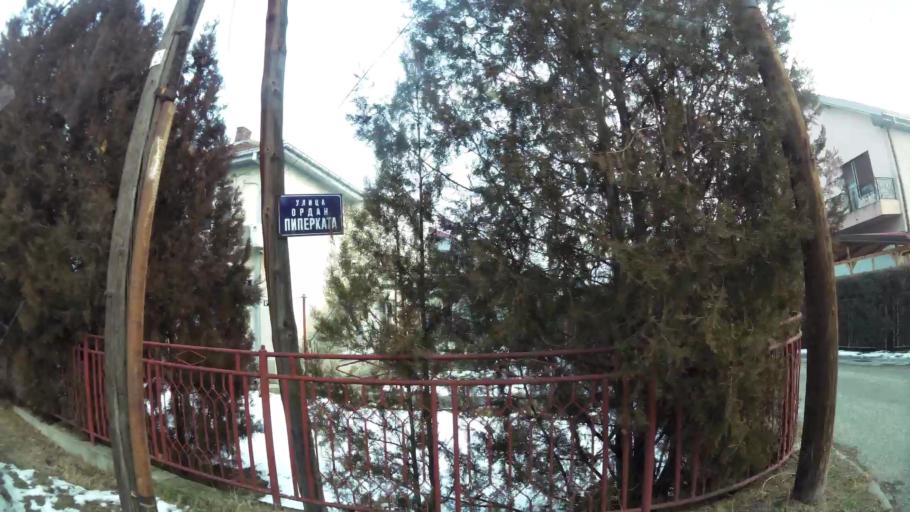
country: MK
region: Kisela Voda
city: Kisela Voda
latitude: 41.9961
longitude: 21.5040
